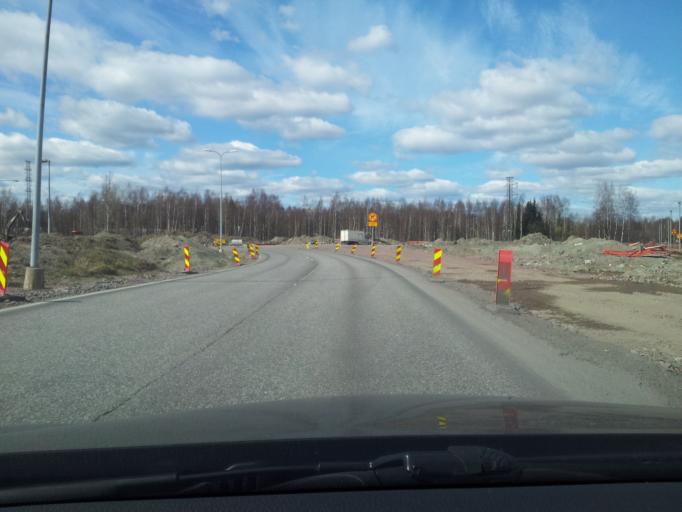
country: FI
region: Uusimaa
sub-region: Helsinki
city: Kilo
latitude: 60.1844
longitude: 24.7765
